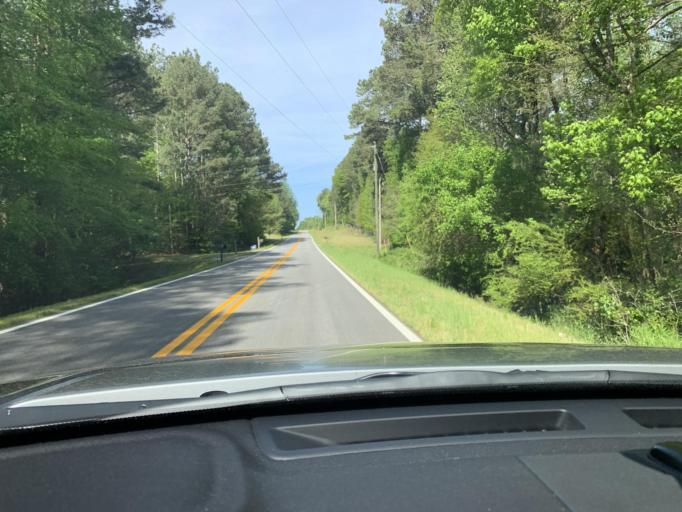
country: US
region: Georgia
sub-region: Oconee County
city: Watkinsville
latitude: 33.8164
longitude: -83.3806
